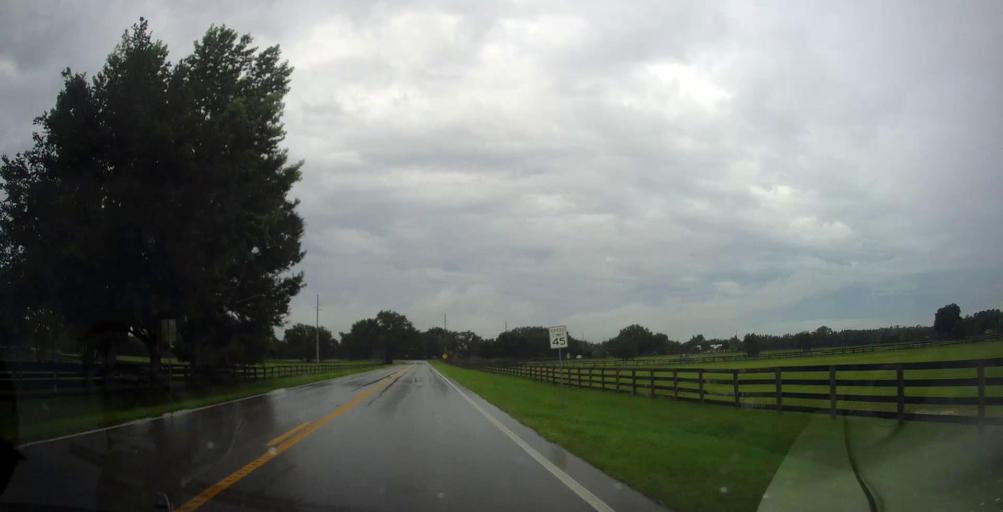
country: US
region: Florida
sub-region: Marion County
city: Citra
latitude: 29.3331
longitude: -82.2072
